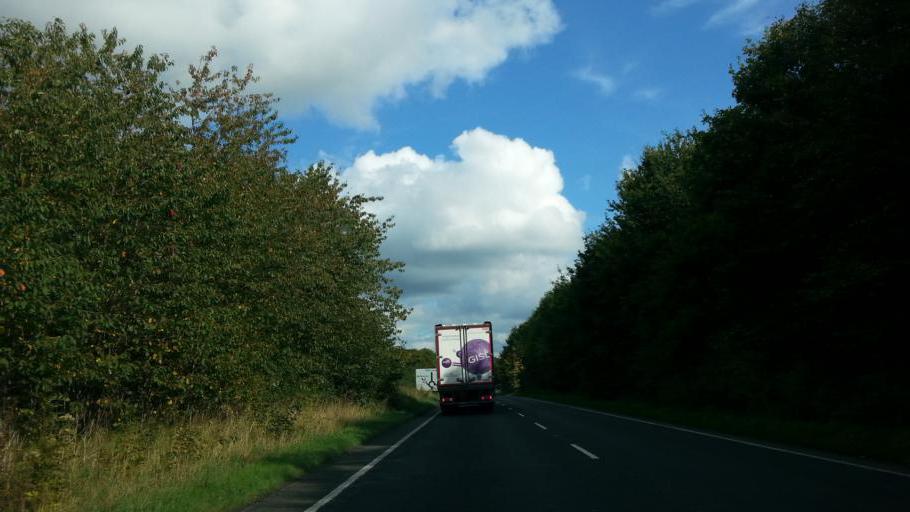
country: GB
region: England
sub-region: Derbyshire
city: Etwall
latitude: 52.8899
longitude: -1.5960
